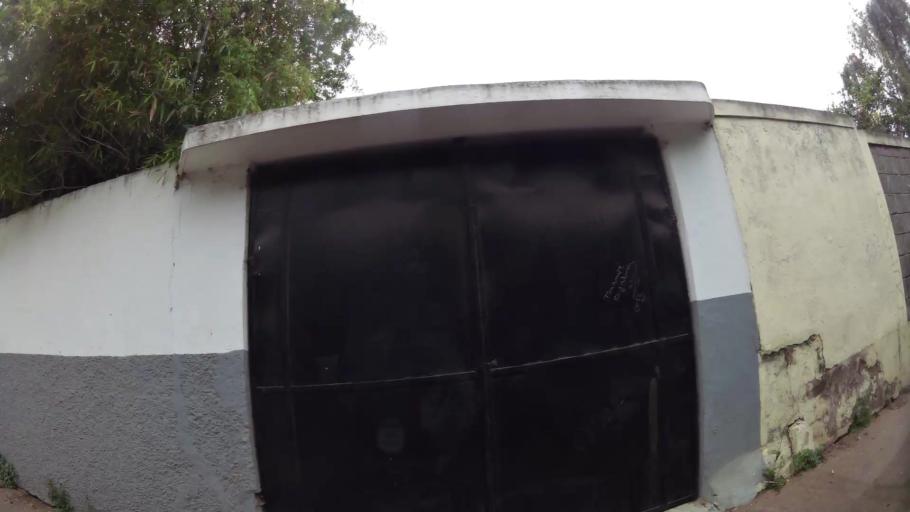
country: MA
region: Rabat-Sale-Zemmour-Zaer
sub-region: Rabat
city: Rabat
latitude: 33.9866
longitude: -6.8245
